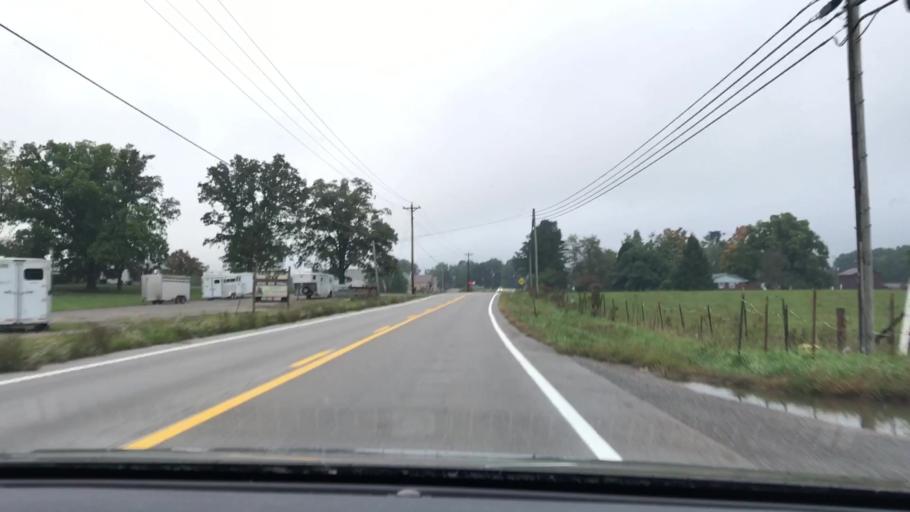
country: US
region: Tennessee
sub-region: Fentress County
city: Grimsley
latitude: 36.2164
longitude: -85.0137
